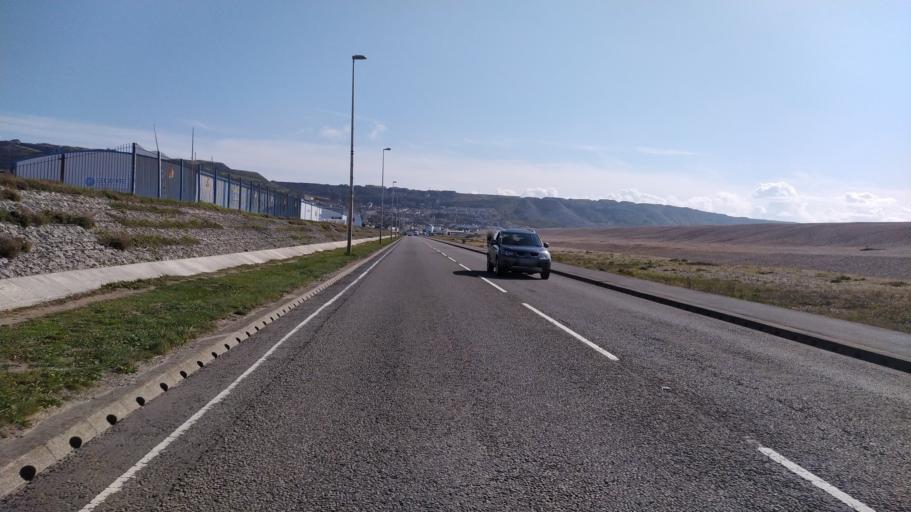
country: GB
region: England
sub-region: Dorset
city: Portland
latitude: 50.5693
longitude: -2.4577
